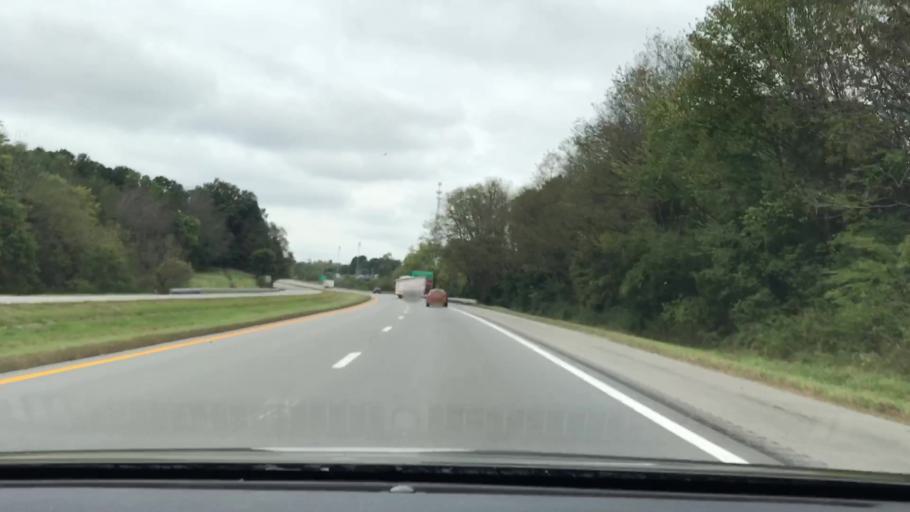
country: US
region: Kentucky
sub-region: Adair County
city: Columbia
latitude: 37.0908
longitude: -85.2920
